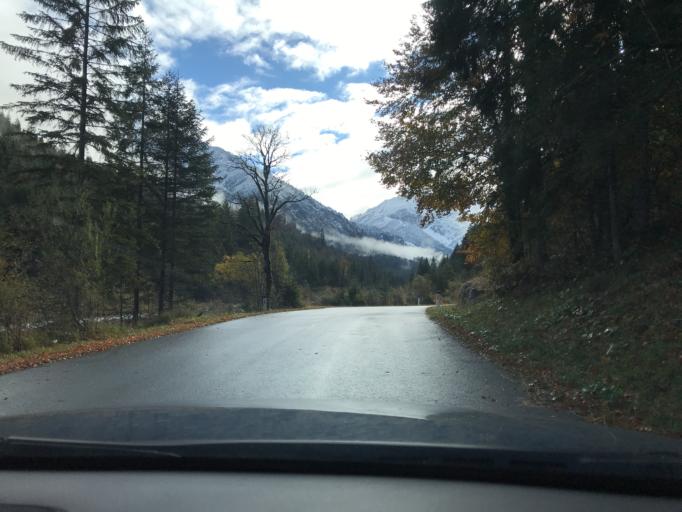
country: AT
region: Tyrol
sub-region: Politischer Bezirk Innsbruck Land
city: Gnadenwald
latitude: 47.4492
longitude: 11.5447
